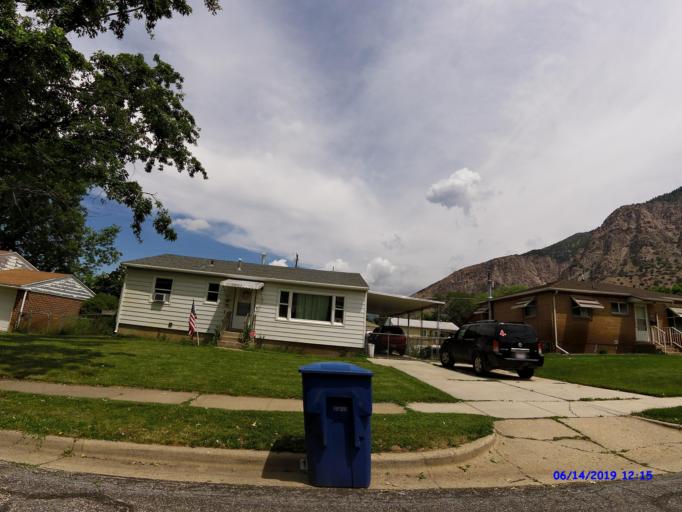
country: US
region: Utah
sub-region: Weber County
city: Ogden
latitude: 41.2575
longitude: -111.9513
